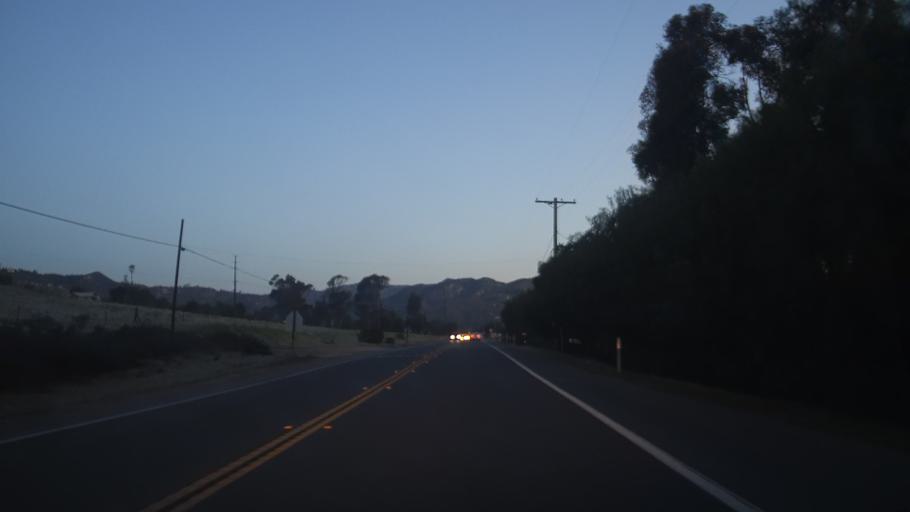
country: US
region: California
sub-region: San Diego County
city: Crest
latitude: 32.7829
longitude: -116.8467
